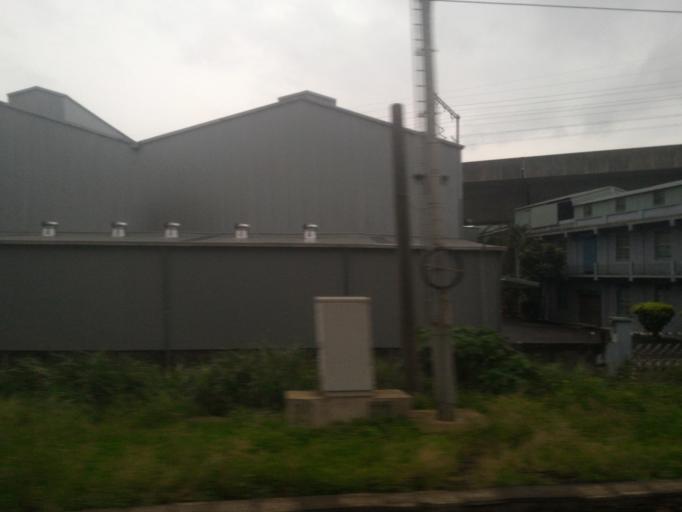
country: TW
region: Taipei
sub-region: Taipei
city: Banqiao
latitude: 25.0037
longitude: 121.4323
